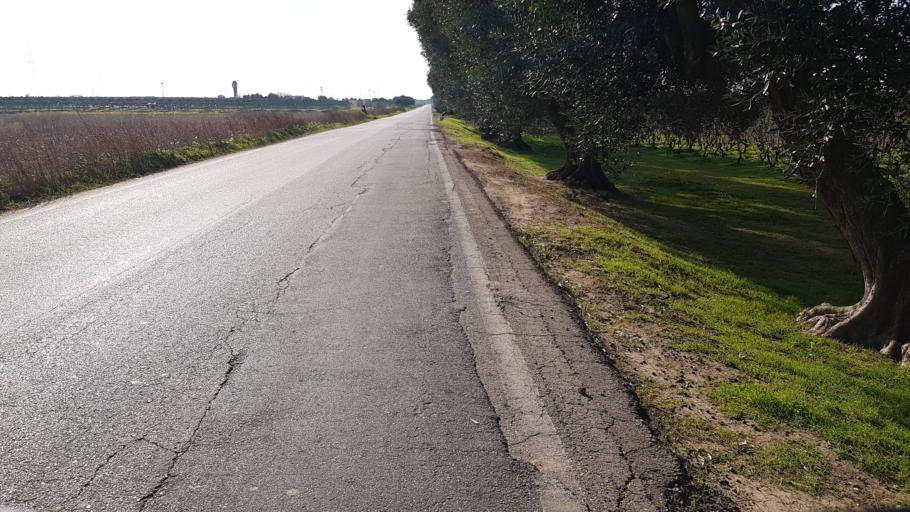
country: IT
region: Apulia
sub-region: Provincia di Brindisi
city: La Rosa
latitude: 40.5858
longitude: 17.9026
